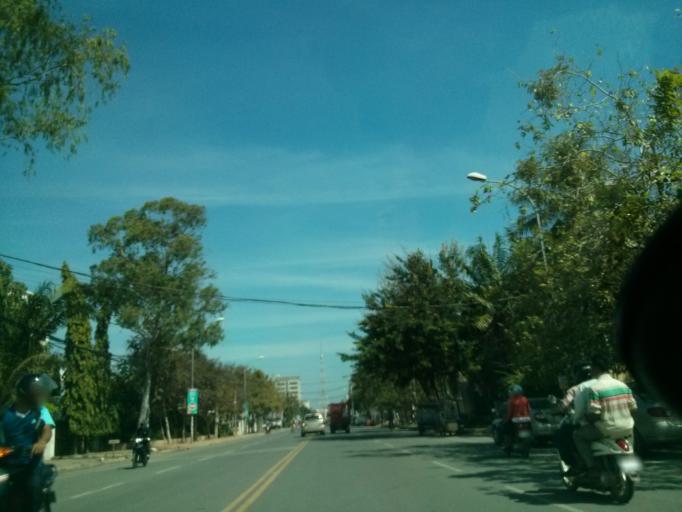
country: KH
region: Phnom Penh
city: Phnom Penh
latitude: 11.5790
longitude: 104.8947
